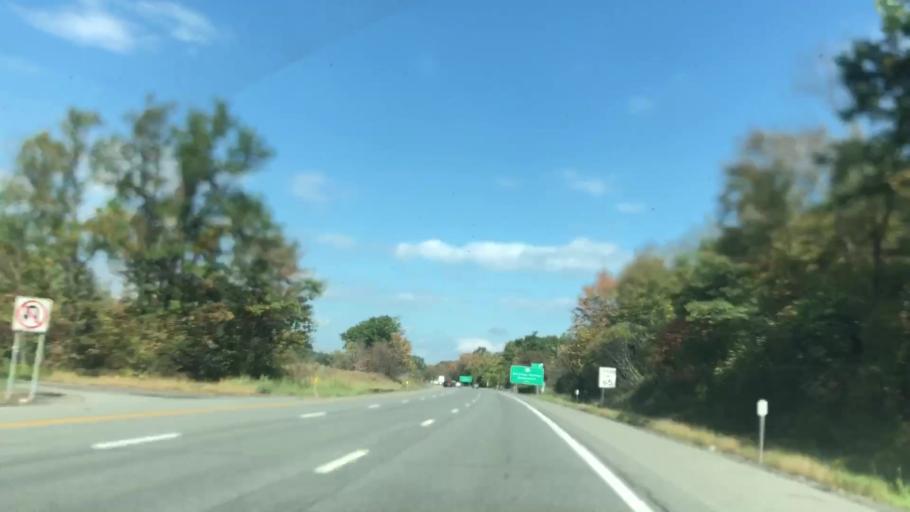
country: US
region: New York
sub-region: Saratoga County
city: Saratoga Springs
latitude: 43.0771
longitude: -73.7487
